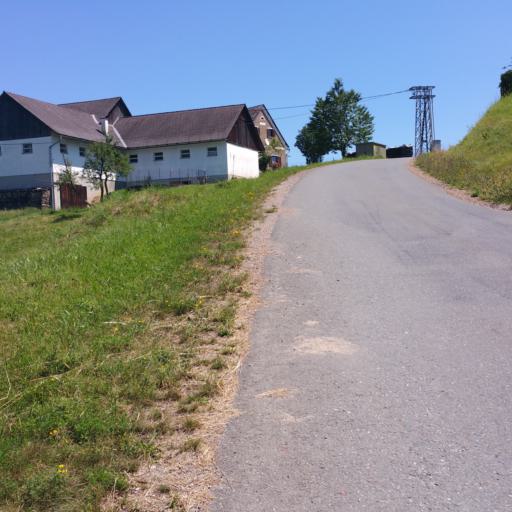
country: AT
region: Styria
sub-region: Politischer Bezirk Leibnitz
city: Gleinstatten
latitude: 46.7306
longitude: 15.3573
